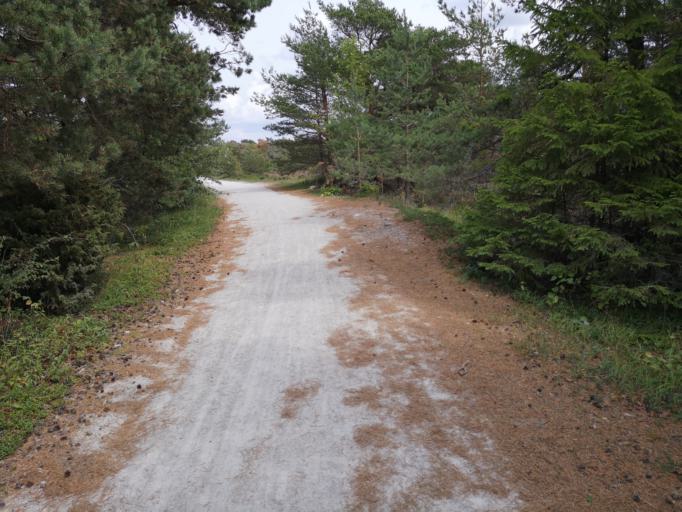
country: SE
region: Gotland
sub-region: Gotland
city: Vibble
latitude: 57.6155
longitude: 18.2596
